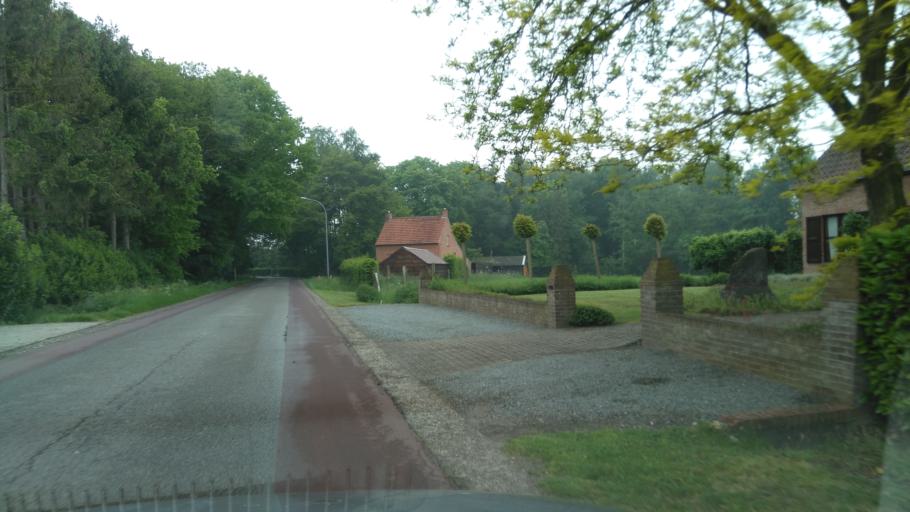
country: BE
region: Flanders
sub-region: Provincie Antwerpen
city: Baarle-Hertog
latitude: 51.3889
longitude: 4.8903
